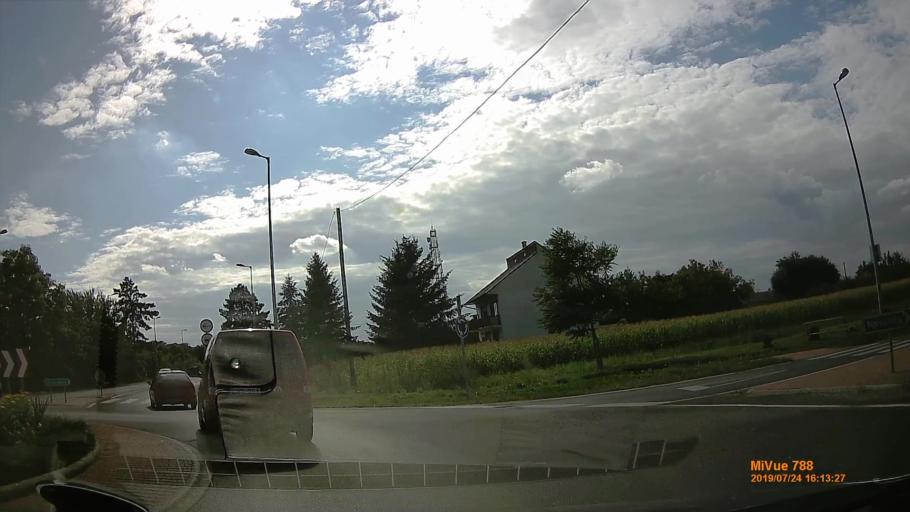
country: HU
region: Szabolcs-Szatmar-Bereg
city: Nyirpazony
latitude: 47.9493
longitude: 21.8041
